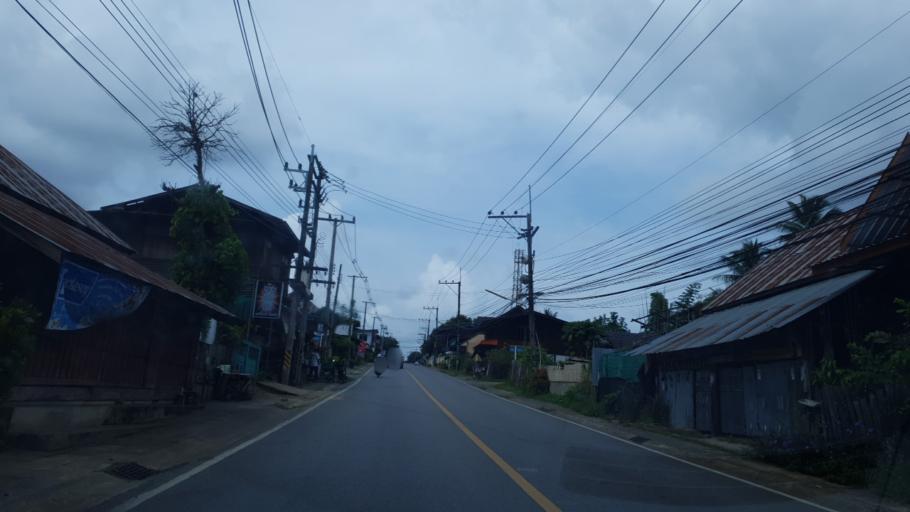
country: TH
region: Mae Hong Son
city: Khun Yuam
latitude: 18.8207
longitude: 97.9366
